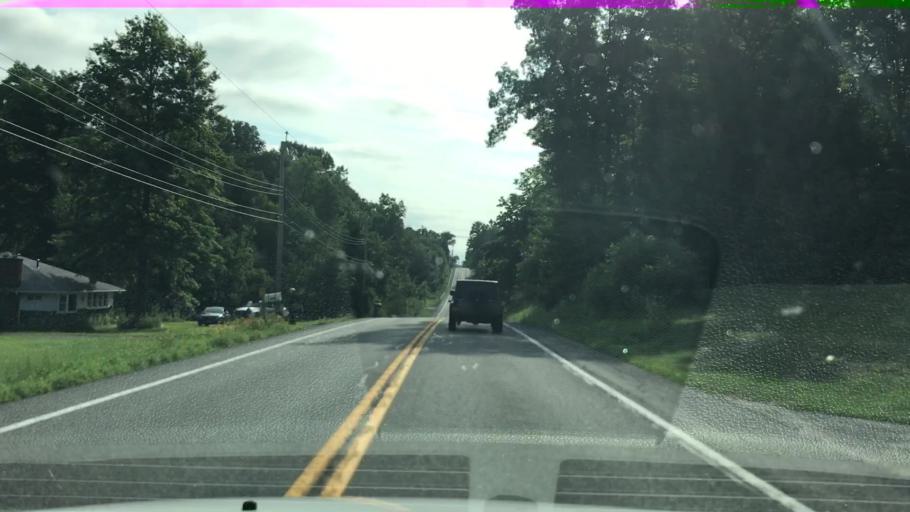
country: US
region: New York
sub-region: Erie County
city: Town Line
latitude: 42.8562
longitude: -78.5849
